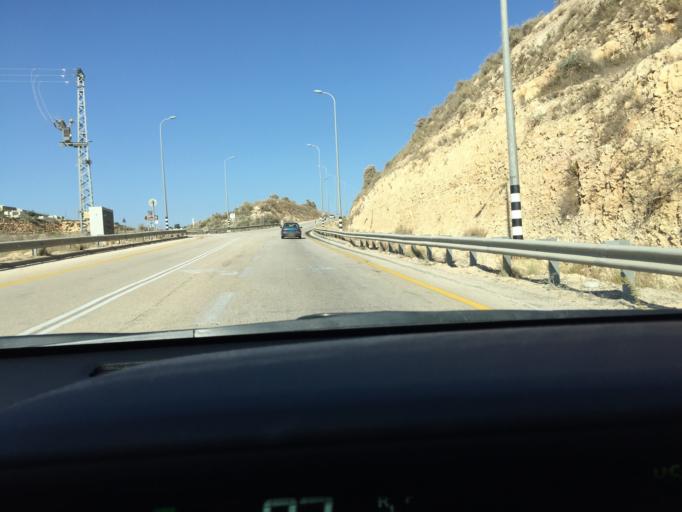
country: PS
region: West Bank
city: Rafat
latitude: 32.0654
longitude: 35.0512
